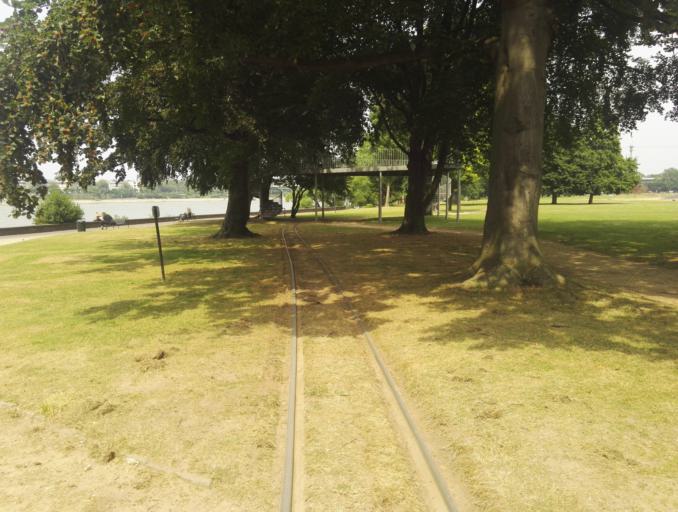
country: DE
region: North Rhine-Westphalia
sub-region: Regierungsbezirk Koln
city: Deutz
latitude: 50.9478
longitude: 6.9718
